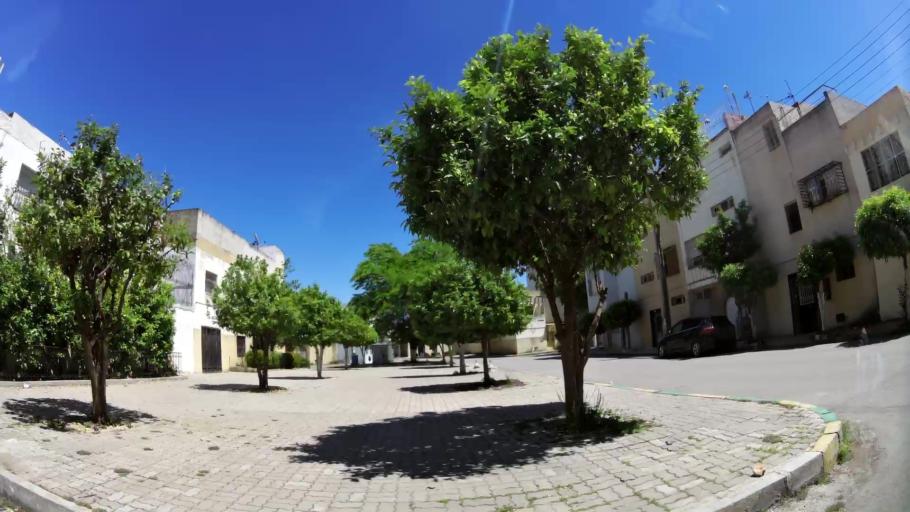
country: MA
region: Fes-Boulemane
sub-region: Fes
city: Fes
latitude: 34.0225
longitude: -5.0054
